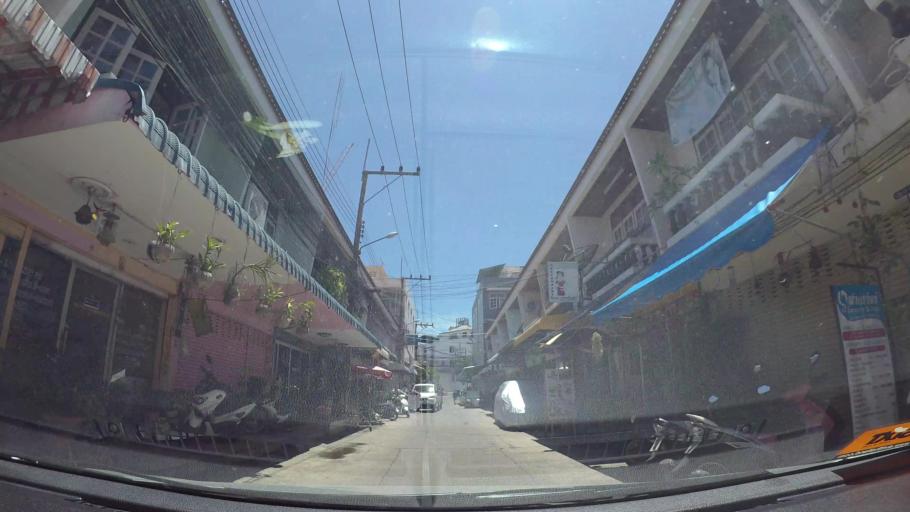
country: TH
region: Chon Buri
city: Phatthaya
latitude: 12.9327
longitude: 100.8921
